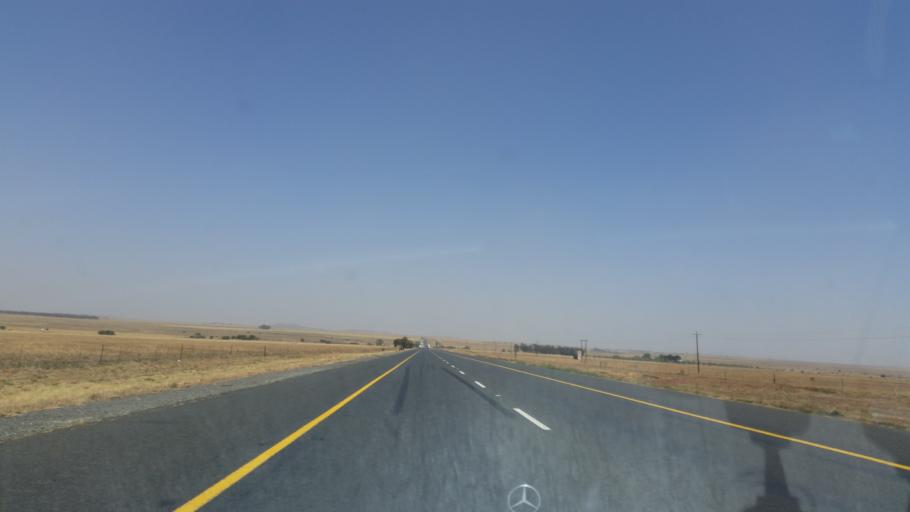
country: ZA
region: Orange Free State
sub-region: Lejweleputswa District Municipality
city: Brandfort
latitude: -28.7213
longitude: 26.7710
